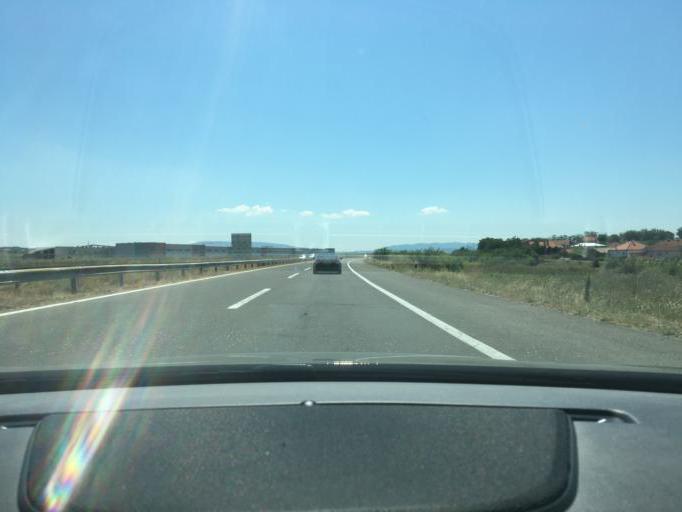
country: MK
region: Ilinden
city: Marino
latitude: 41.9958
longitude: 21.5919
